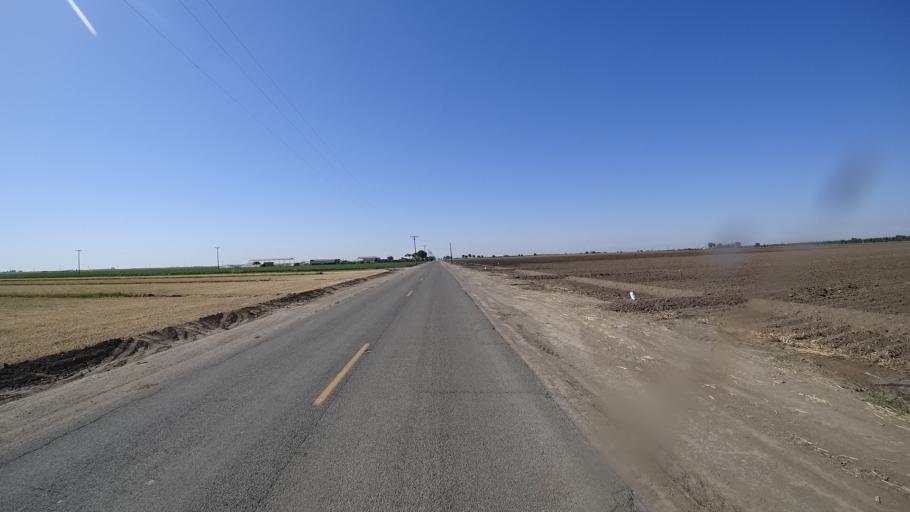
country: US
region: California
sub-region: Kings County
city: Home Garden
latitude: 36.2611
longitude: -119.5474
